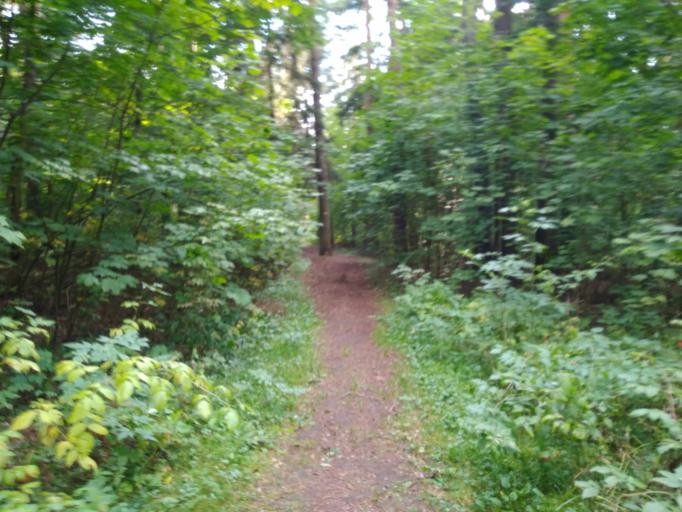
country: RU
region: Moskovskaya
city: Zhukovskiy
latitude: 55.5863
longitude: 38.1175
